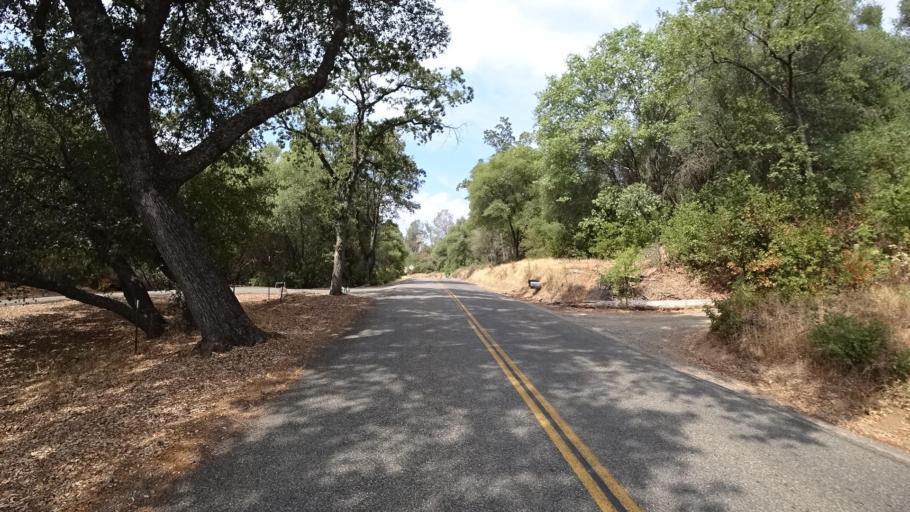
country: US
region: California
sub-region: Mariposa County
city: Midpines
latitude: 37.5103
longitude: -119.9099
